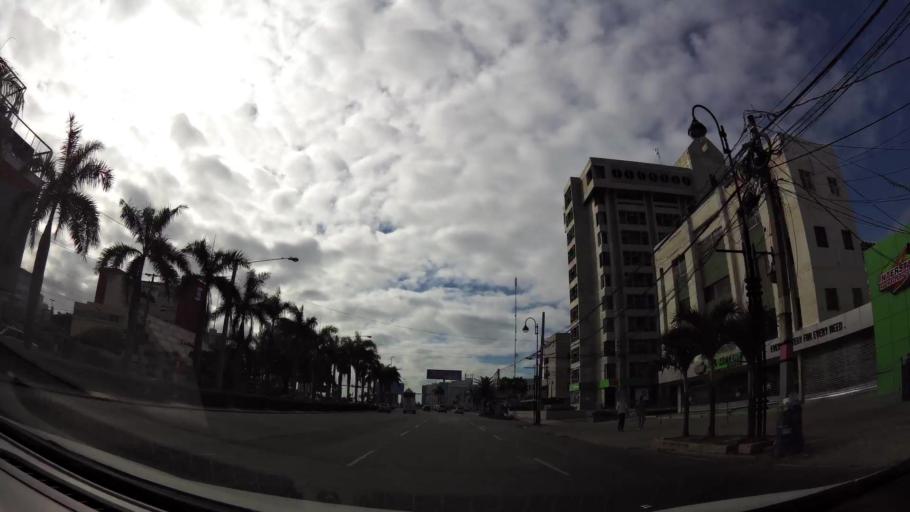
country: DO
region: Nacional
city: La Julia
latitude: 18.4640
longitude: -69.9370
